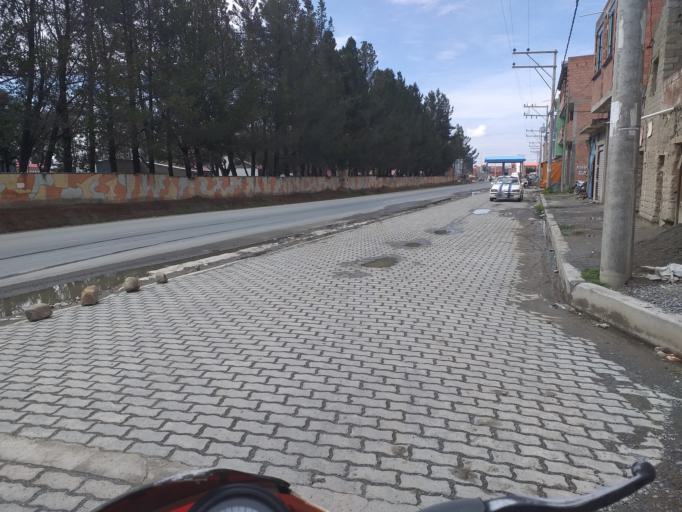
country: BO
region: La Paz
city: Achacachi
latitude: -16.0335
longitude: -68.6887
